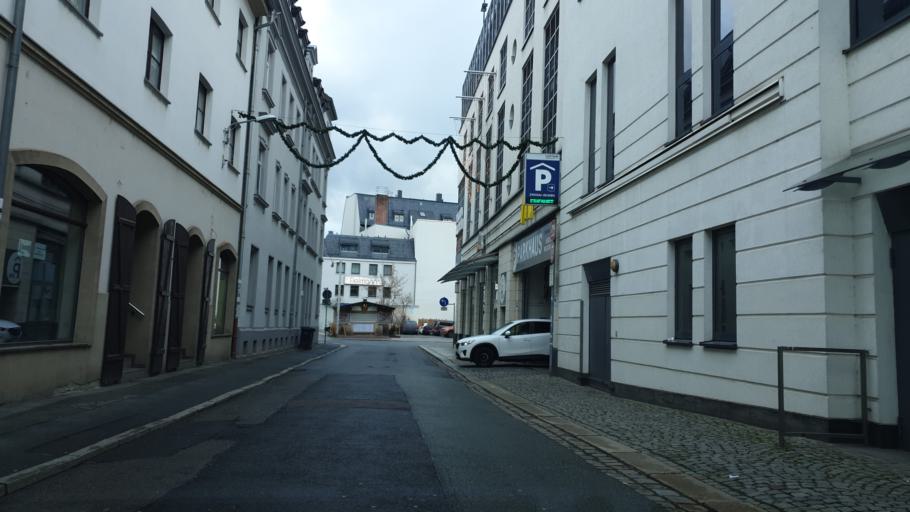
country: DE
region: Saxony
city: Zwickau
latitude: 50.7200
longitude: 12.4944
